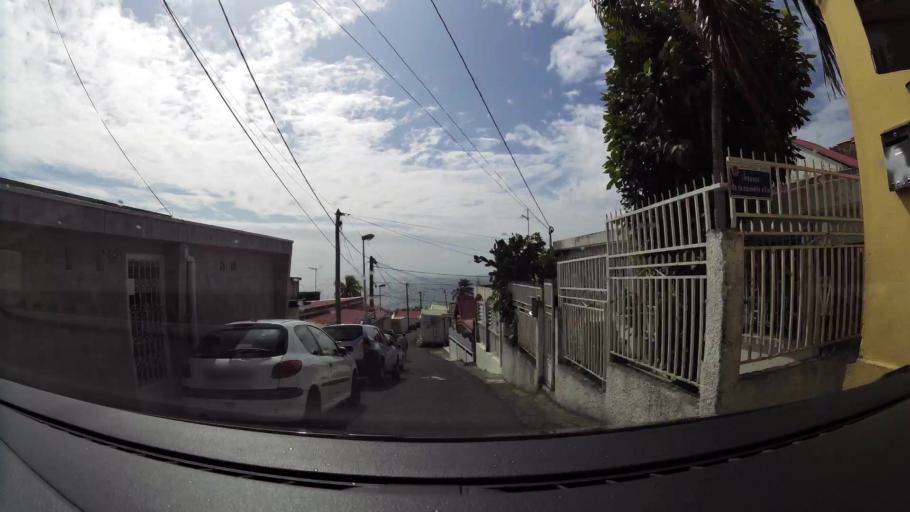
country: GP
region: Guadeloupe
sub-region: Guadeloupe
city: Basse-Terre
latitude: 16.0020
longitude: -61.7349
